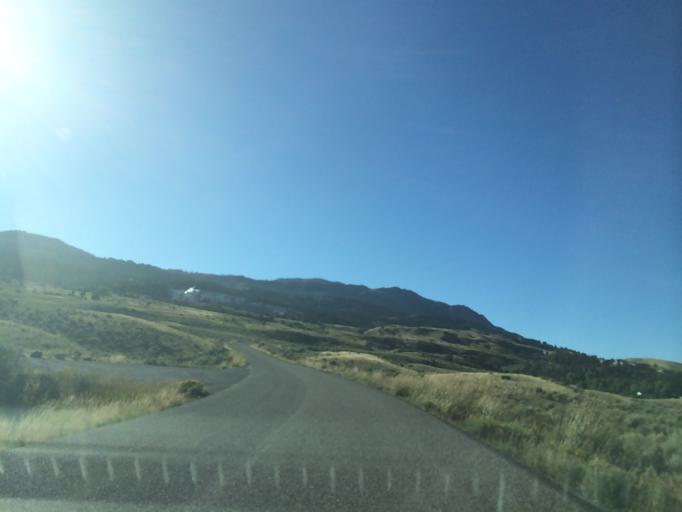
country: US
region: Montana
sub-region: Gallatin County
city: West Yellowstone
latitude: 44.9646
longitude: -110.6874
